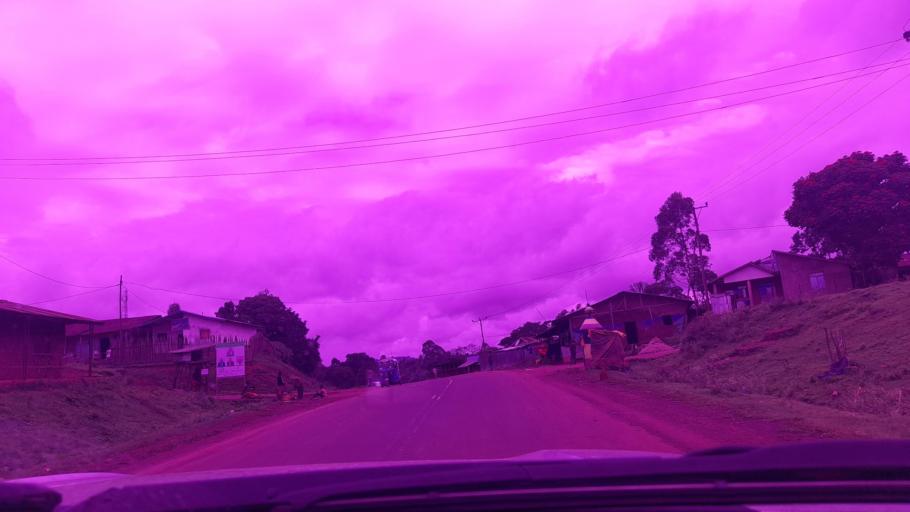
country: ET
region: Southern Nations, Nationalities, and People's Region
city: Bonga
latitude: 7.2967
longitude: 35.9877
